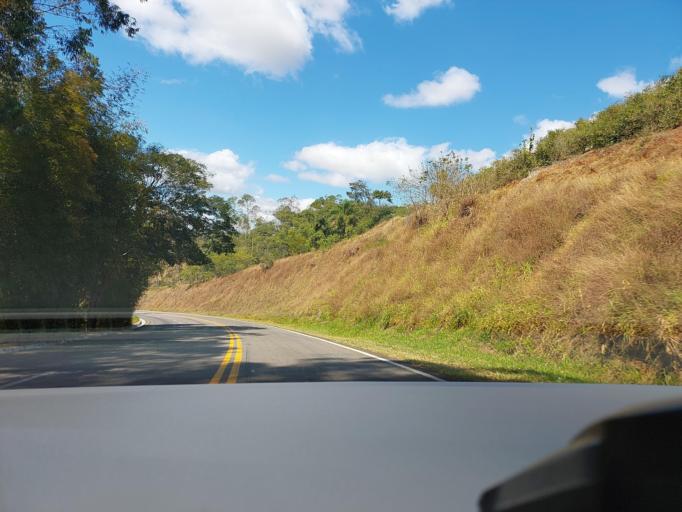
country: BR
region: Minas Gerais
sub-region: Mirai
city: Mirai
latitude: -21.0430
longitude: -42.5318
